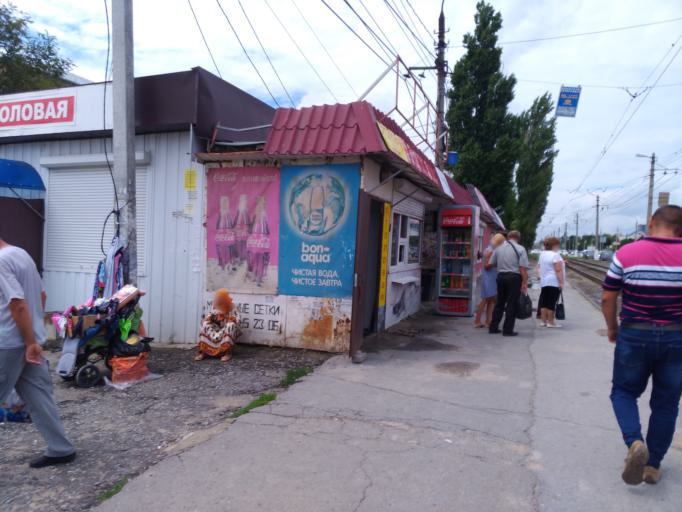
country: RU
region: Volgograd
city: Volgograd
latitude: 48.7154
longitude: 44.4907
